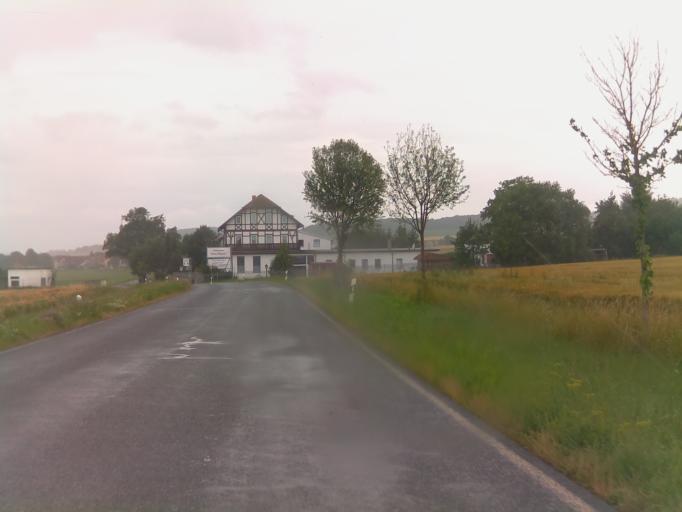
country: DE
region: Thuringia
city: Stadtilm
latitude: 50.7531
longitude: 11.1371
